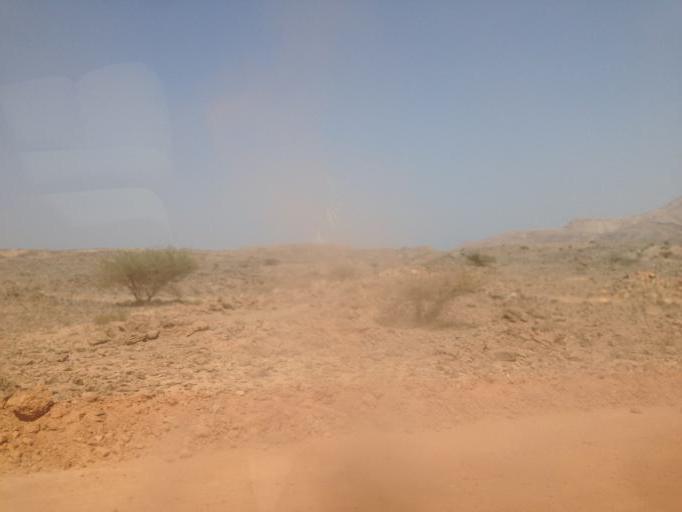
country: OM
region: Ash Sharqiyah
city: Al Qabil
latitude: 23.0714
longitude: 58.9574
